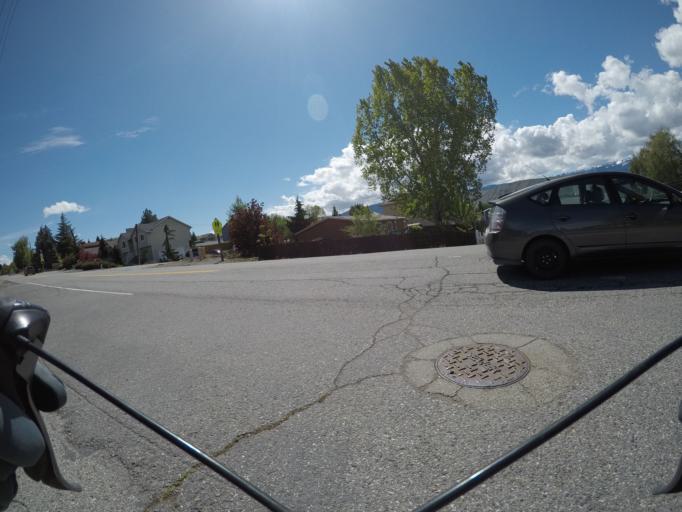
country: US
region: Washington
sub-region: Douglas County
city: East Wenatchee Bench
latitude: 47.4205
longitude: -120.2784
